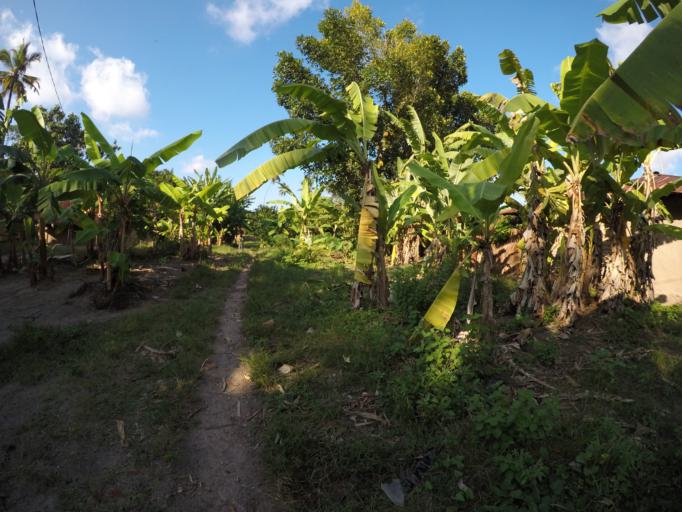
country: TZ
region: Pemba South
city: Mtambile
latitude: -5.3875
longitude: 39.7350
